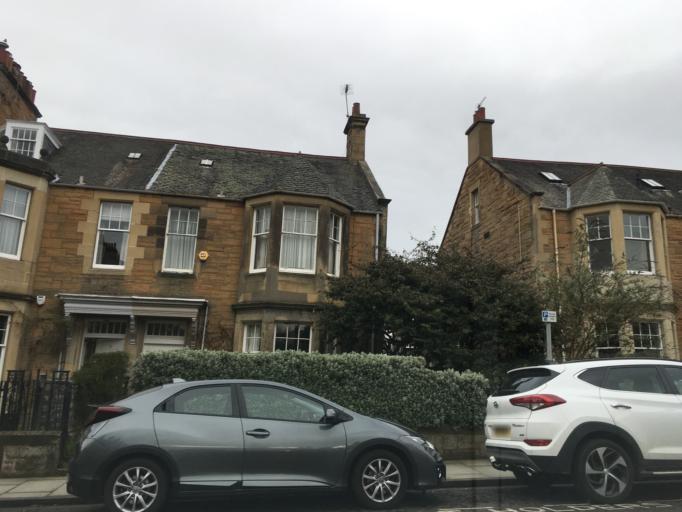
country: GB
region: Scotland
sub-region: Edinburgh
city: Edinburgh
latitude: 55.9263
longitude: -3.2025
